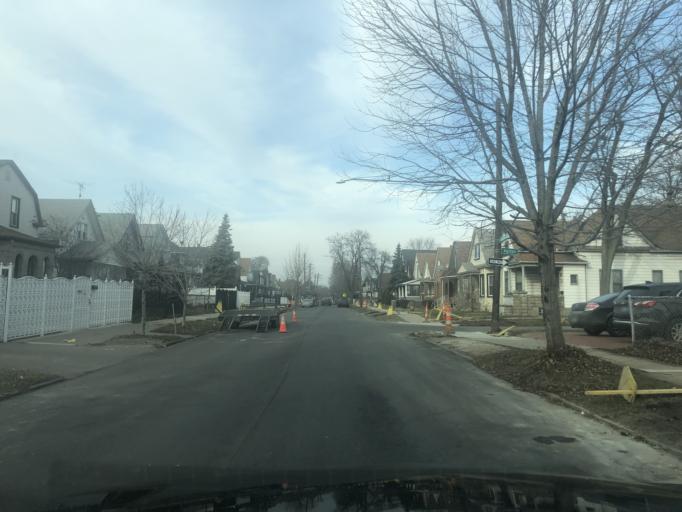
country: US
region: Michigan
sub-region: Wayne County
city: River Rouge
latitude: 42.3121
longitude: -83.1026
